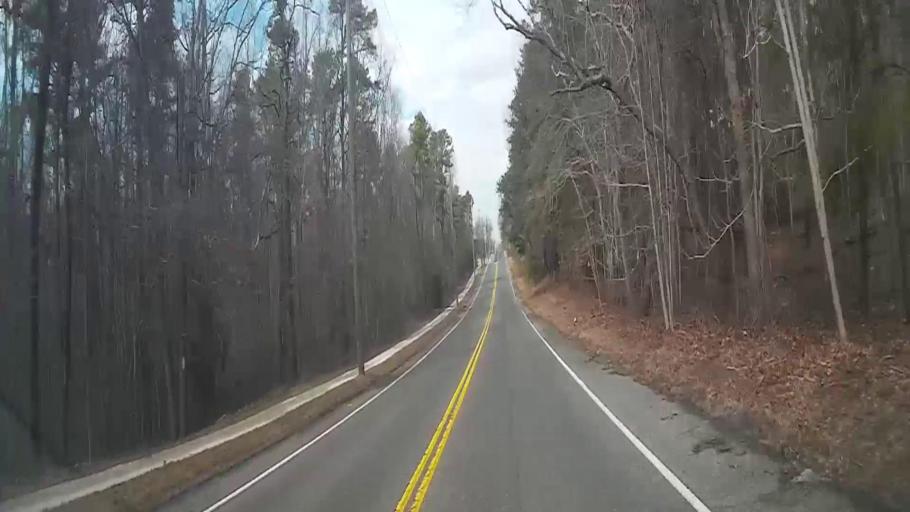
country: US
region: New Jersey
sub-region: Gloucester County
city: Turnersville
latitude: 39.7799
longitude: -75.0338
